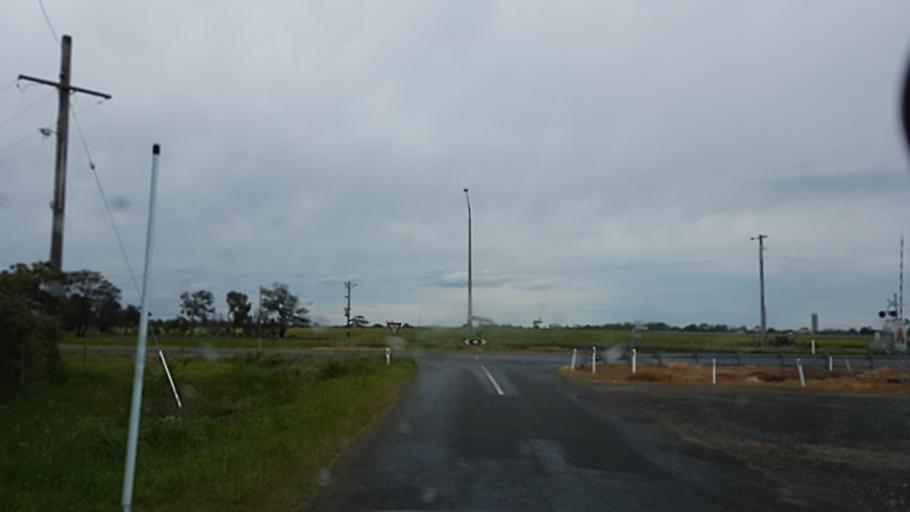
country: AU
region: Victoria
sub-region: Ballarat North
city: Mount Clear
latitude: -37.7750
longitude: 144.0264
